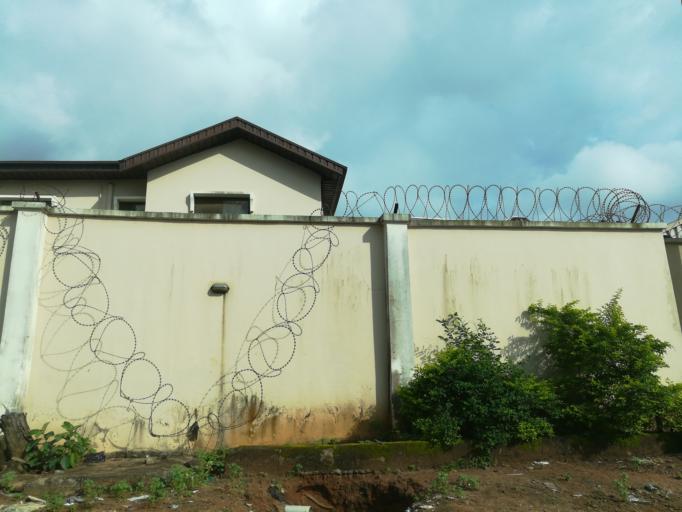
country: NG
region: Lagos
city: Ebute Ikorodu
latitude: 6.5963
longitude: 3.5053
